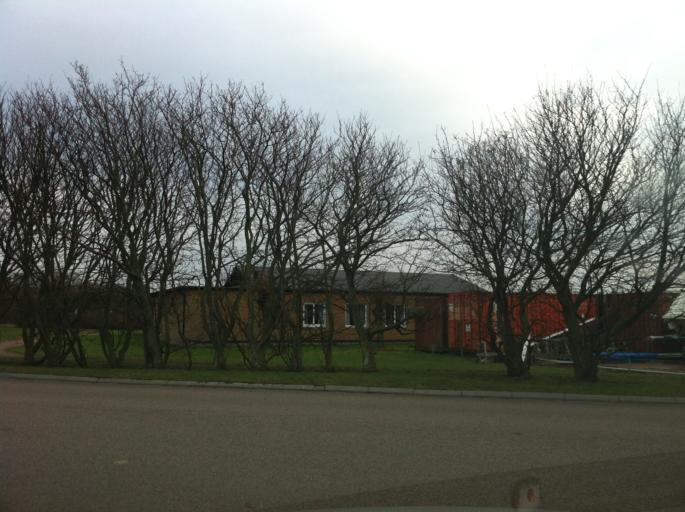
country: SE
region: Skane
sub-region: Hoganas Kommun
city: Hoganas
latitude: 56.2003
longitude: 12.5481
